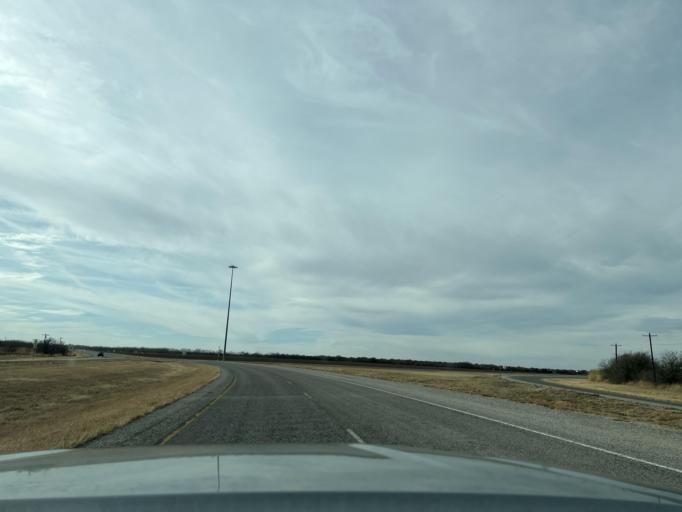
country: US
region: Texas
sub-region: Jones County
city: Stamford
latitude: 32.7667
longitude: -99.5881
